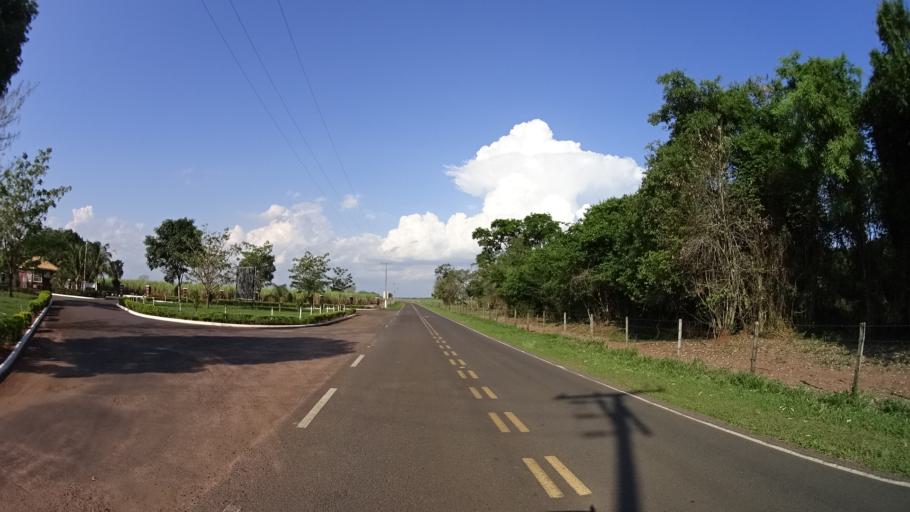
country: BR
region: Sao Paulo
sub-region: Urupes
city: Urupes
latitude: -21.3950
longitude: -49.5111
